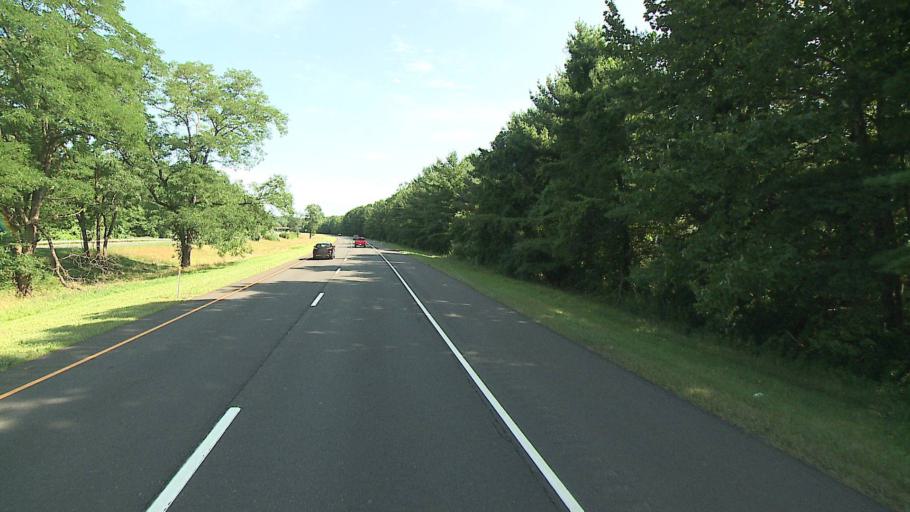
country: US
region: Connecticut
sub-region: Fairfield County
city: Danbury
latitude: 41.4486
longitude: -73.3953
